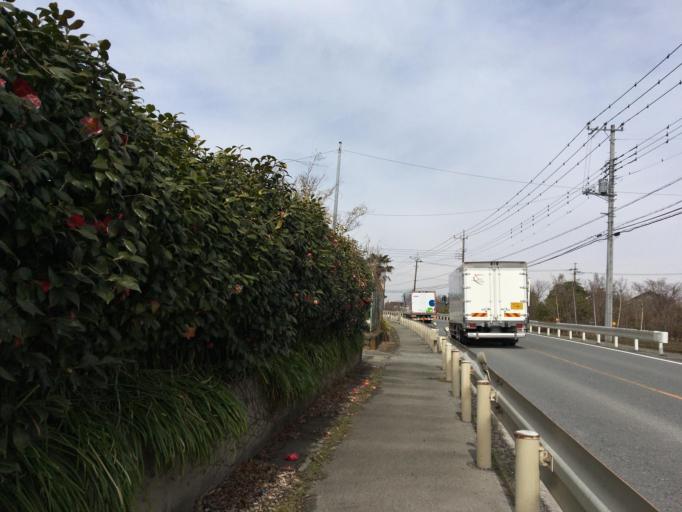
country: JP
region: Saitama
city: Yorii
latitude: 36.1468
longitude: 139.2065
